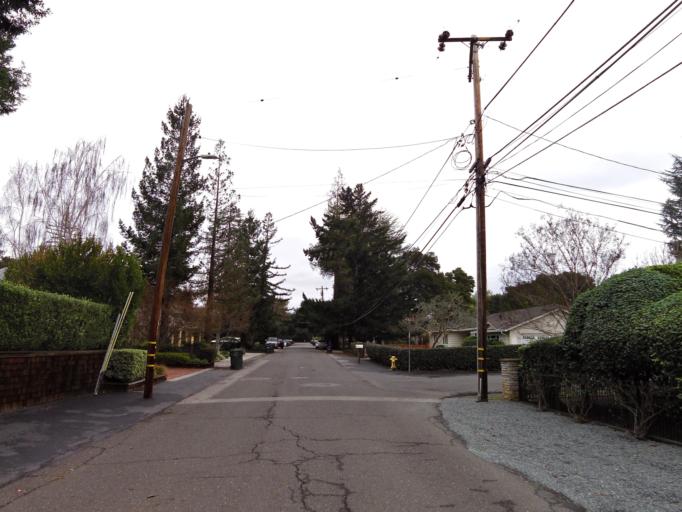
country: US
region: California
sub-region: Santa Clara County
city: Loyola
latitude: 37.3576
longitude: -122.0897
